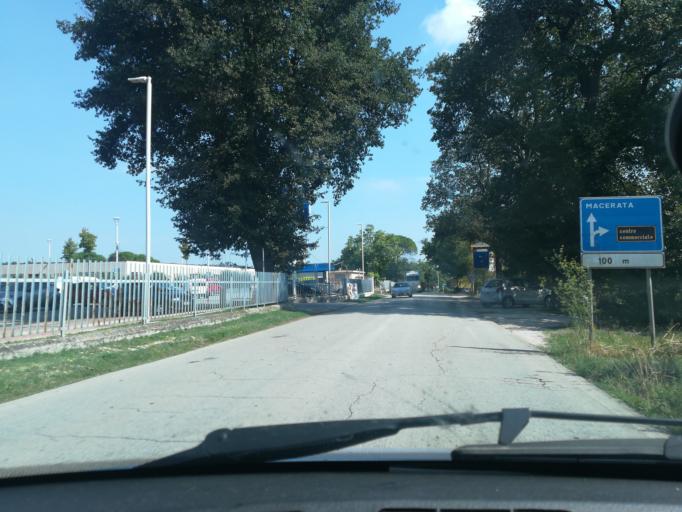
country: IT
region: The Marches
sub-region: Provincia di Macerata
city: Pollenza
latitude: 43.2231
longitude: 13.3333
